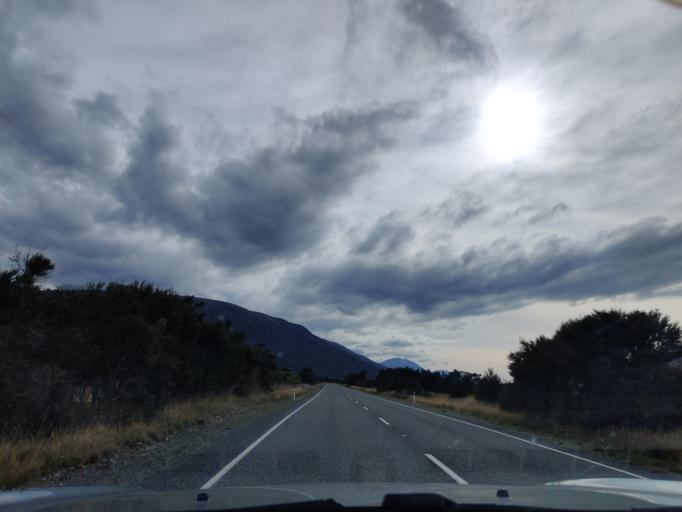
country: NZ
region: Tasman
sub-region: Tasman District
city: Wakefield
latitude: -41.7580
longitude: 172.9821
